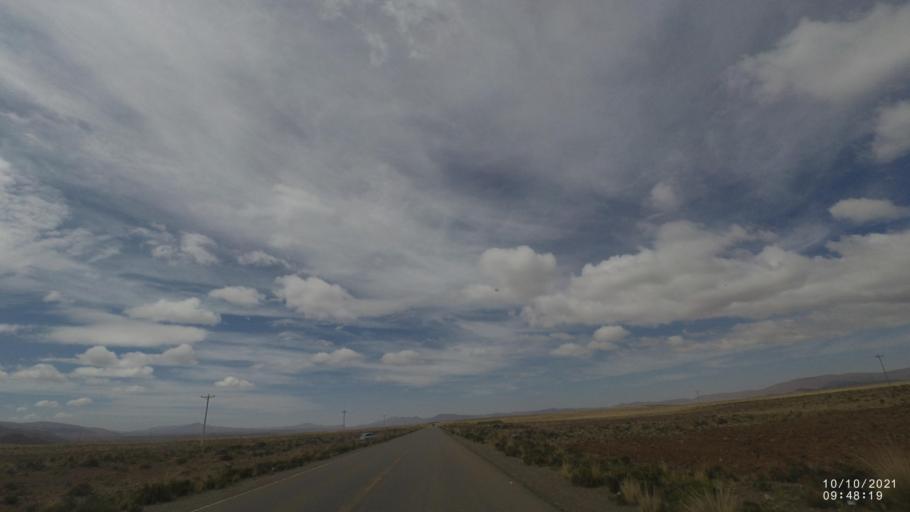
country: BO
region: La Paz
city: Quime
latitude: -17.2077
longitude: -67.3418
